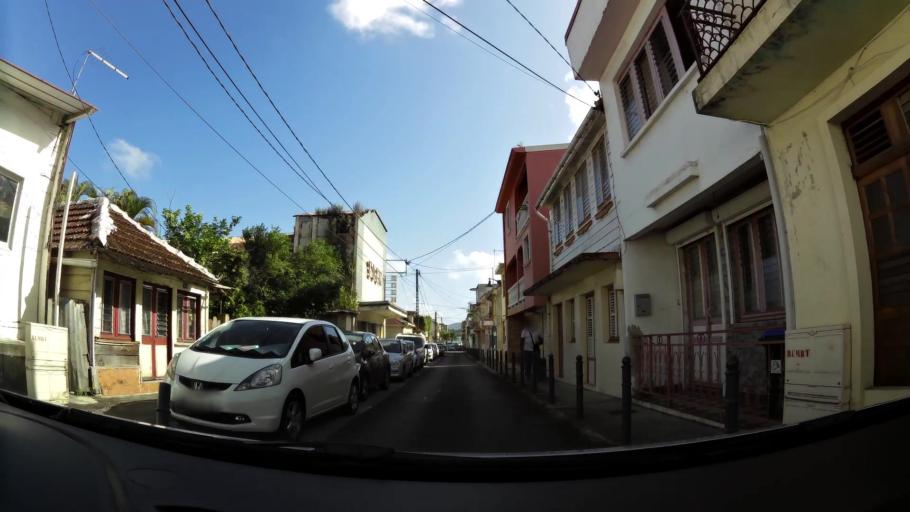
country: MQ
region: Martinique
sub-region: Martinique
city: La Trinite
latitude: 14.7391
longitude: -60.9650
